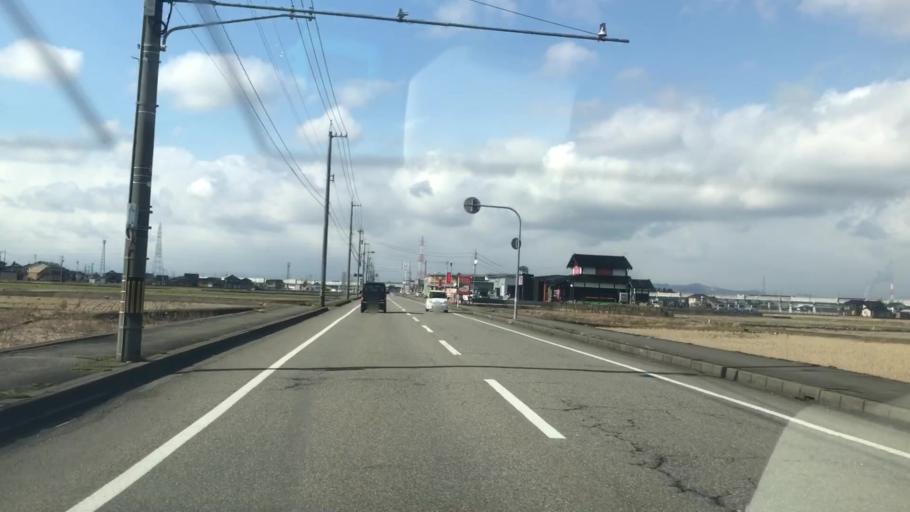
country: JP
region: Toyama
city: Nishishinminato
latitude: 36.7180
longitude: 137.0804
